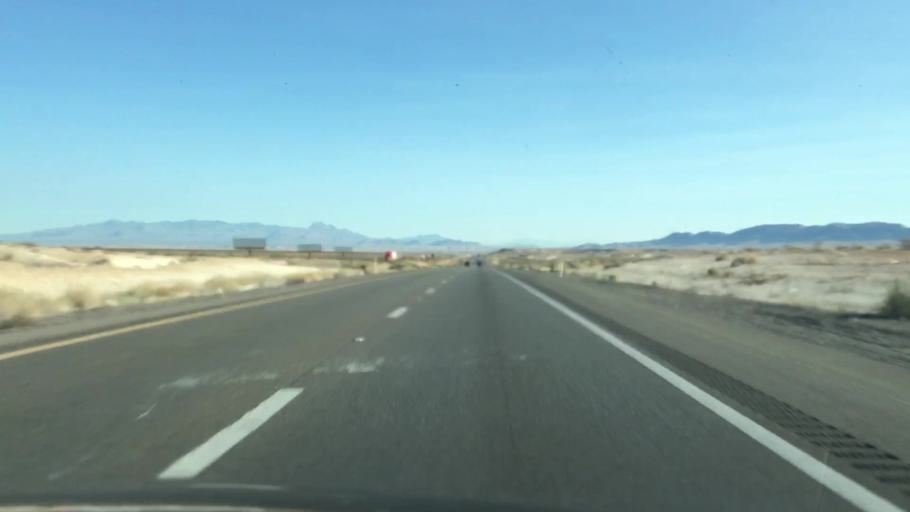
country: US
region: Nevada
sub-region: Clark County
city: Moapa Town
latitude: 36.5228
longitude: -114.7337
